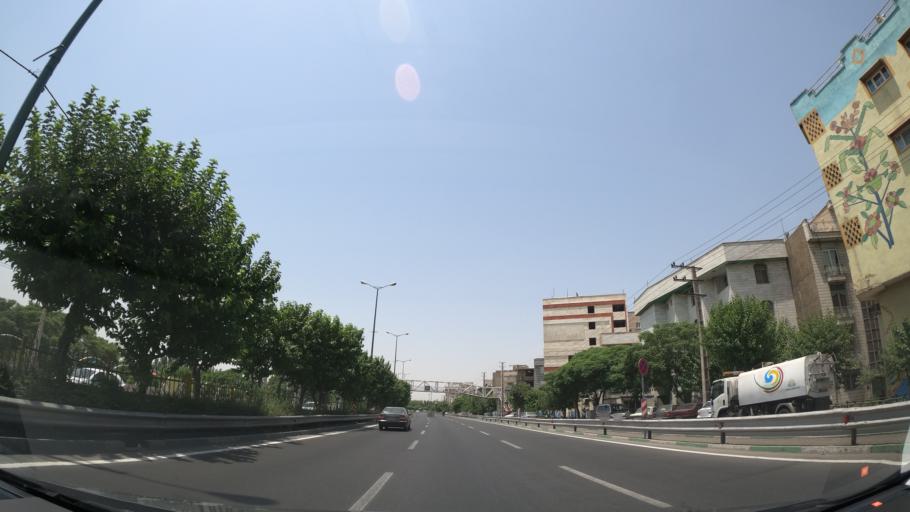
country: IR
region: Tehran
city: Tehran
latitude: 35.6512
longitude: 51.3871
